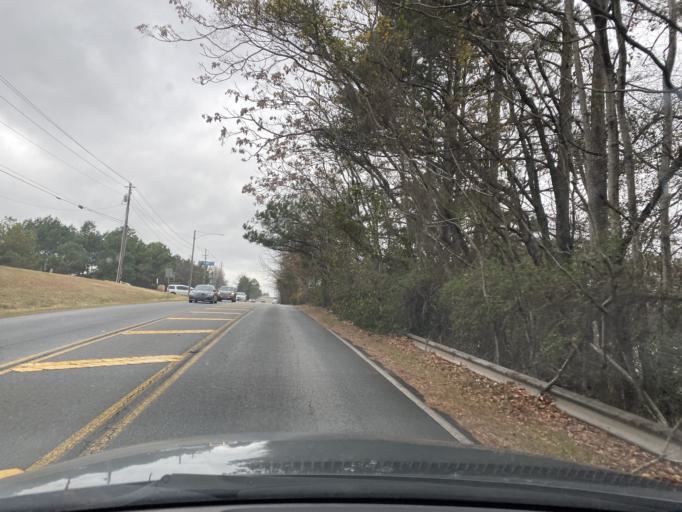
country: US
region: Georgia
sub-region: DeKalb County
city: Redan
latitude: 33.7030
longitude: -84.1640
